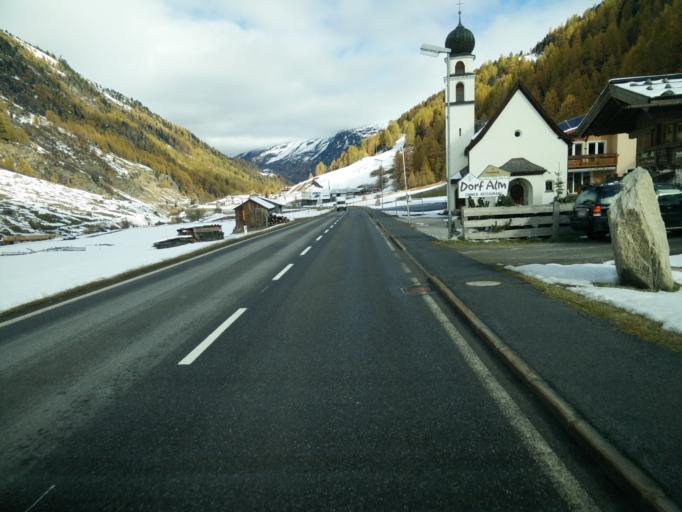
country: AT
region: Tyrol
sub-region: Politischer Bezirk Imst
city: Soelden
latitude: 46.8936
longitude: 11.0401
